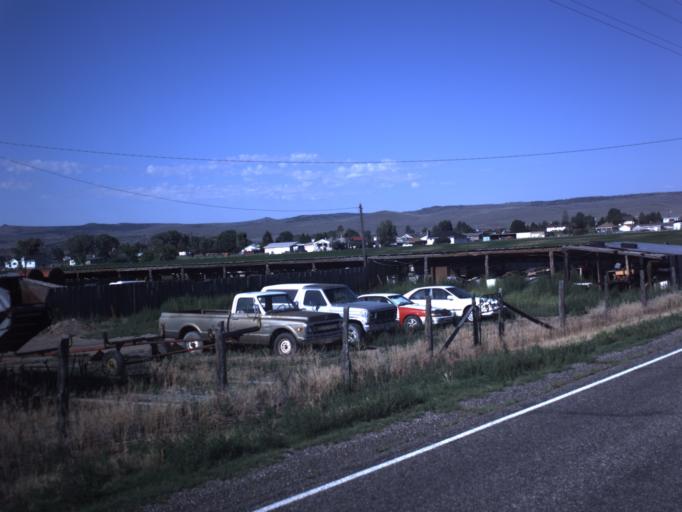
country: US
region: Utah
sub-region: Wayne County
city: Loa
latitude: 38.4117
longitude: -111.6352
